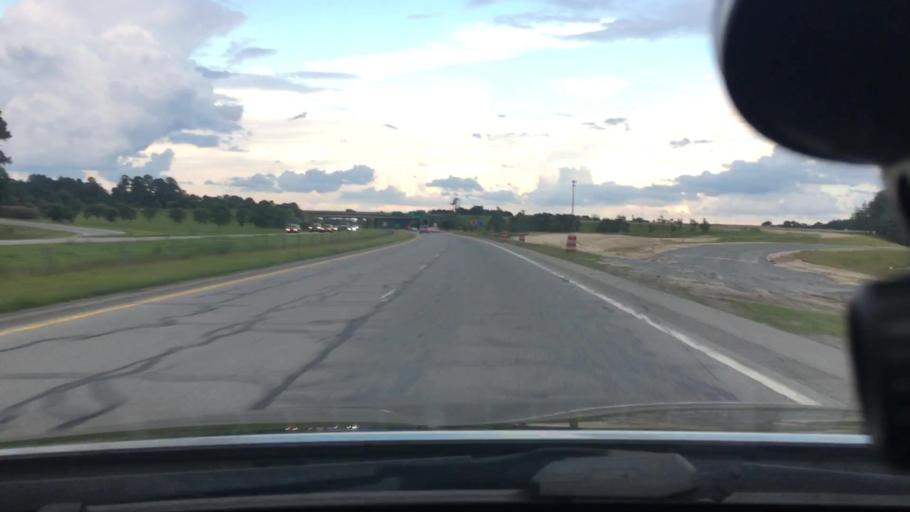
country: US
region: North Carolina
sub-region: Pitt County
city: Summerfield
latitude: 35.6086
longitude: -77.4411
